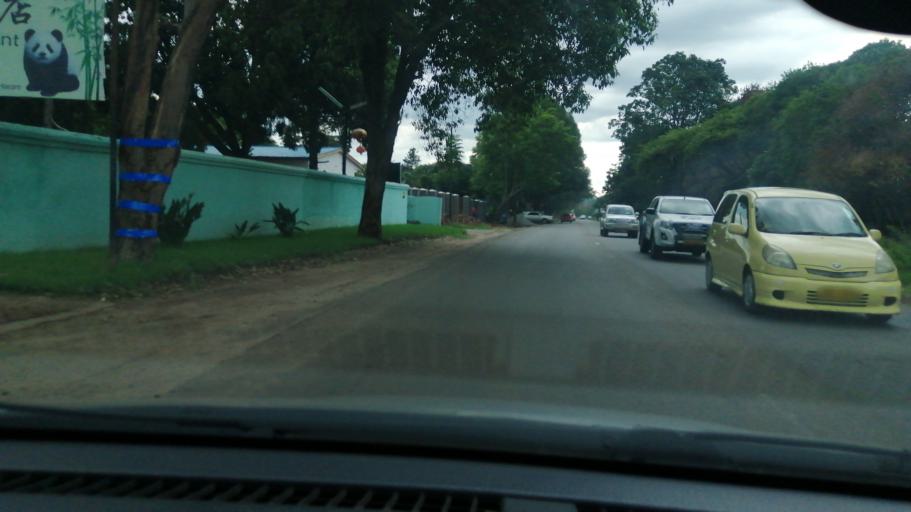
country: ZW
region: Harare
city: Harare
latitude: -17.7906
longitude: 31.0581
